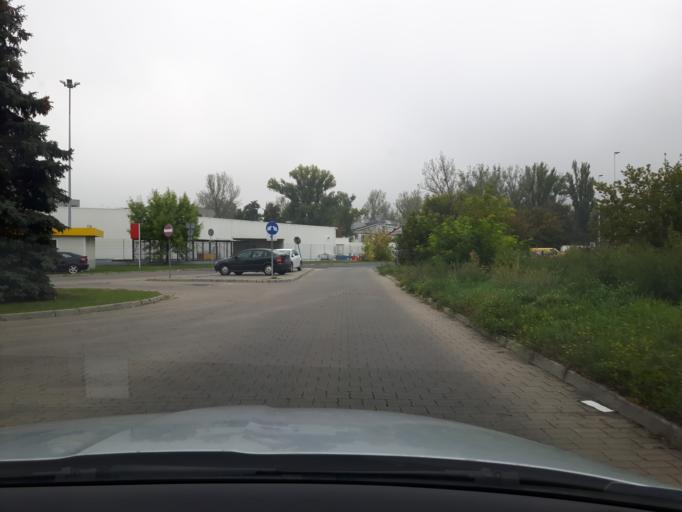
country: PL
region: Masovian Voivodeship
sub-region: Warszawa
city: Praga Polnoc
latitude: 52.2641
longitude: 21.0494
